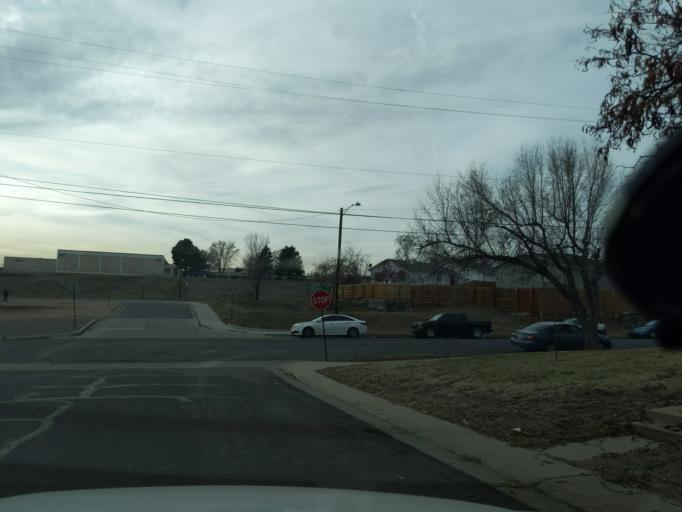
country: US
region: Colorado
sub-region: Adams County
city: Thornton
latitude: 39.8601
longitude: -104.9555
